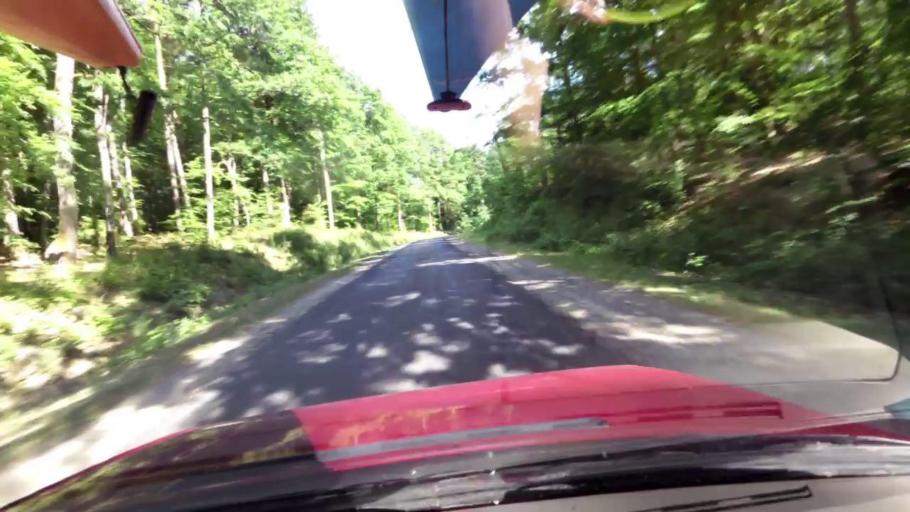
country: PL
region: Pomeranian Voivodeship
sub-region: Powiat slupski
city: Kepice
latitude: 54.1278
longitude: 16.9395
